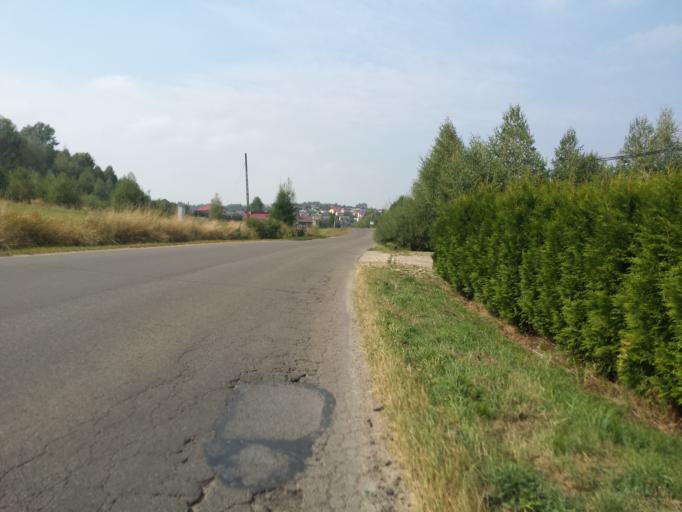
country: PL
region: Subcarpathian Voivodeship
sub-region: Powiat rzeszowski
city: Blazowa
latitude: 49.8762
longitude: 22.0982
